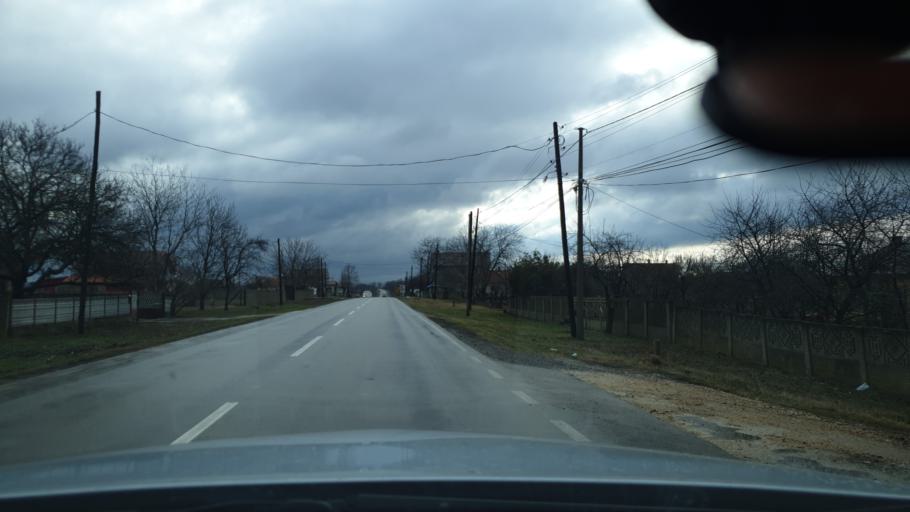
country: RS
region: Central Serbia
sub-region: Branicevski Okrug
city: Malo Crnice
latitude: 44.5620
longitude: 21.2974
